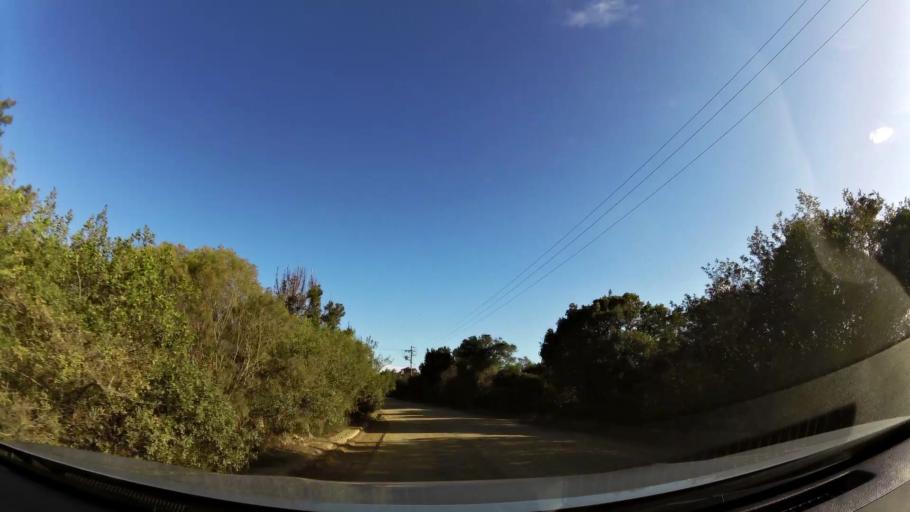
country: ZA
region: Western Cape
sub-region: Eden District Municipality
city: George
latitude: -33.9917
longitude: 22.5623
